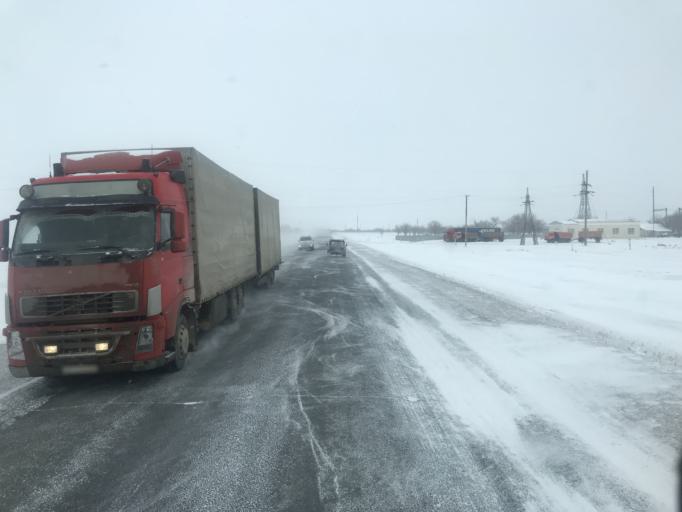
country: KZ
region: Batys Qazaqstan
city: Chapaev
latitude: 50.5158
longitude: 51.0592
